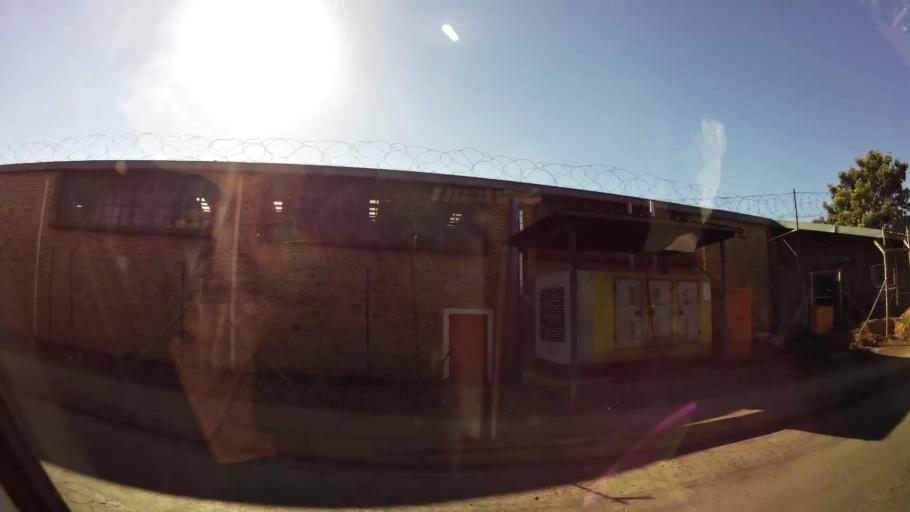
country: ZA
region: Limpopo
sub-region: Mopani District Municipality
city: Tzaneen
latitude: -23.8286
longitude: 30.1649
